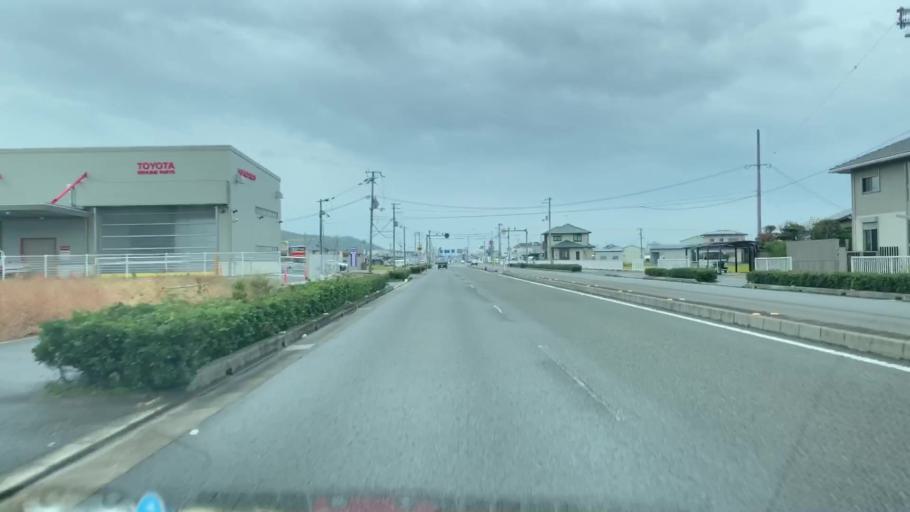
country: JP
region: Wakayama
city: Wakayama-shi
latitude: 34.2387
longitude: 135.2395
